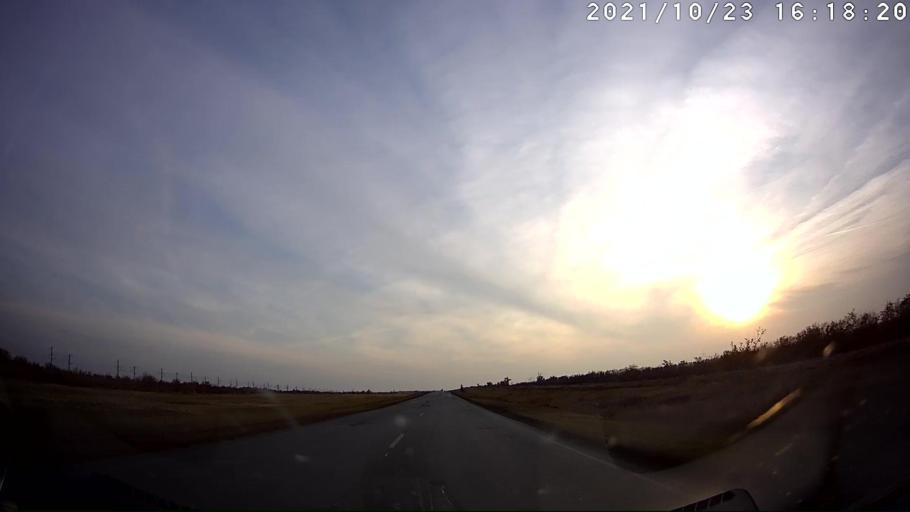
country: RU
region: Volgograd
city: Kotel'nikovo
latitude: 47.9016
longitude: 43.5489
